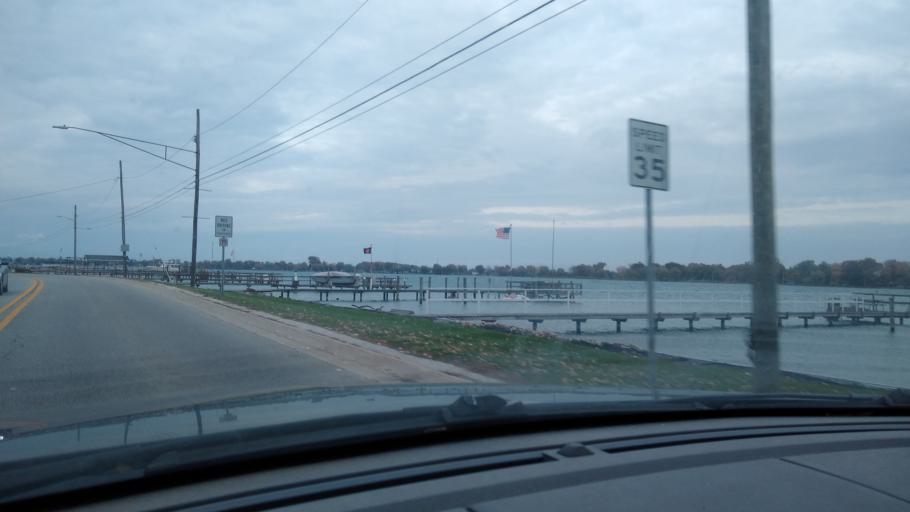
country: CA
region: Ontario
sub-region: Lambton County
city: Walpole Island
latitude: 42.6315
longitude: -82.5168
